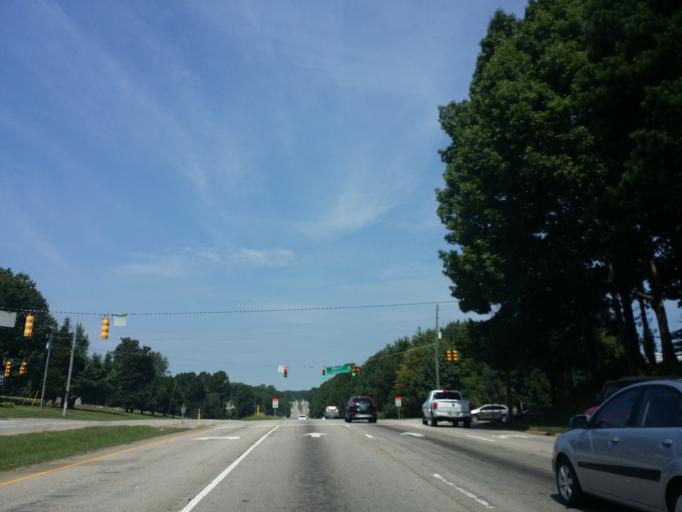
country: US
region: North Carolina
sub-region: Wake County
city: West Raleigh
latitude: 35.8658
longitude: -78.7165
